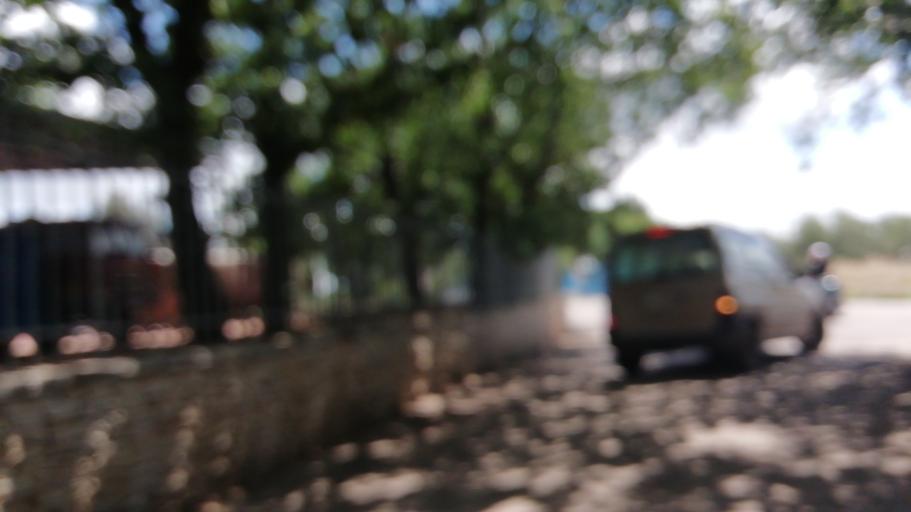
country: IT
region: Apulia
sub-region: Provincia di Bari
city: Corato
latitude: 41.0956
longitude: 16.3450
